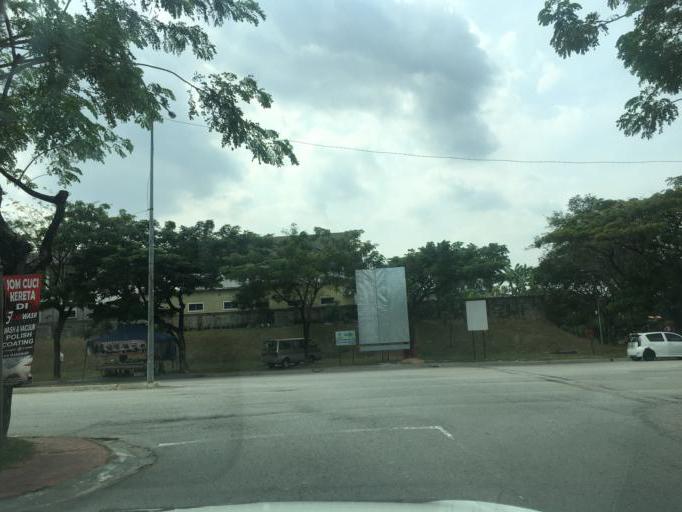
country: MY
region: Selangor
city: Shah Alam
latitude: 3.0812
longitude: 101.4815
